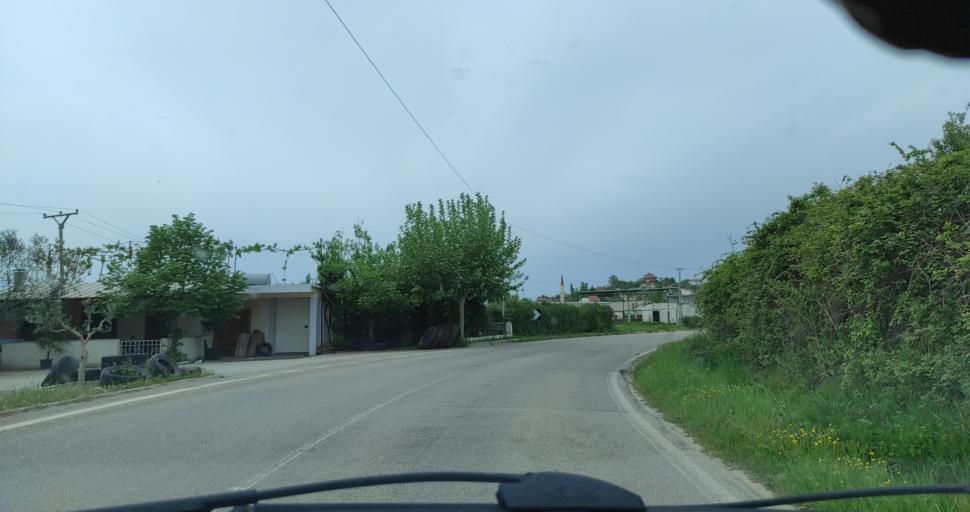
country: AL
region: Lezhe
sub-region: Rrethi i Kurbinit
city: Lac
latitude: 41.6171
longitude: 19.7115
